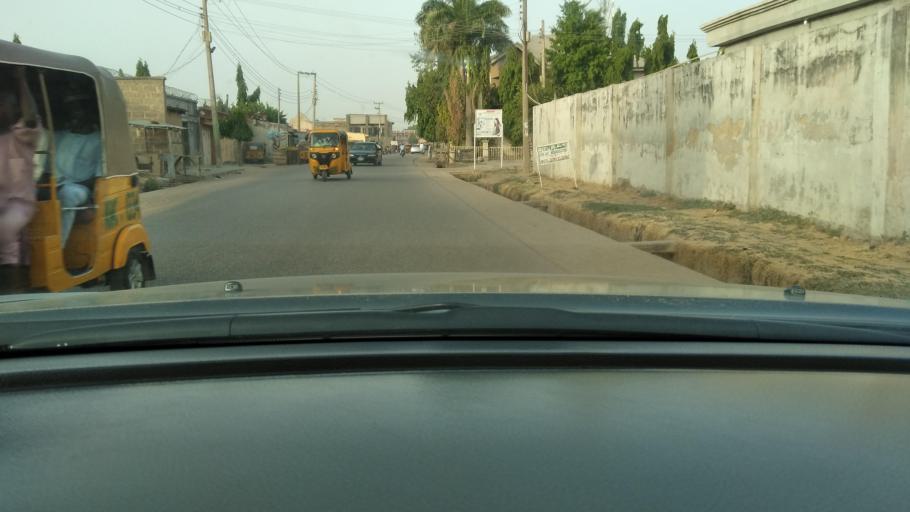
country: NG
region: Kano
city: Kano
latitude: 11.9583
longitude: 8.5230
